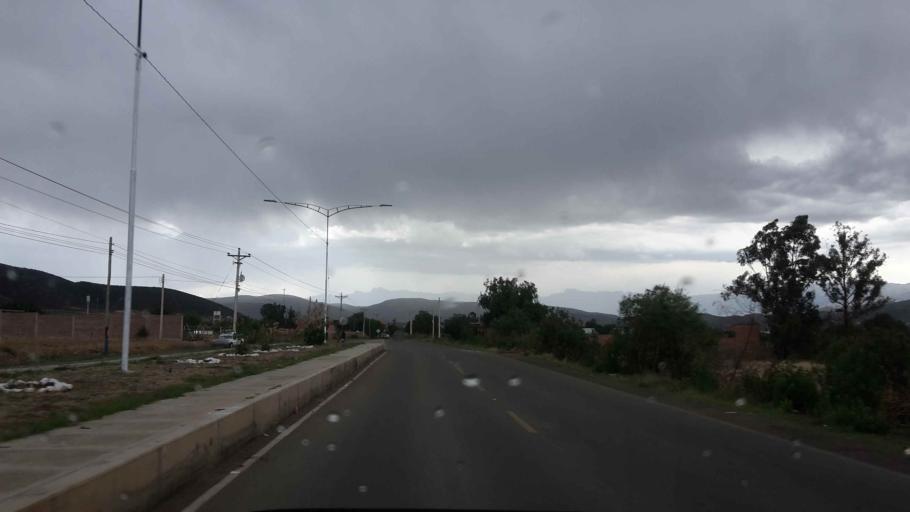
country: BO
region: Cochabamba
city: Tarata
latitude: -17.5934
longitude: -66.0429
